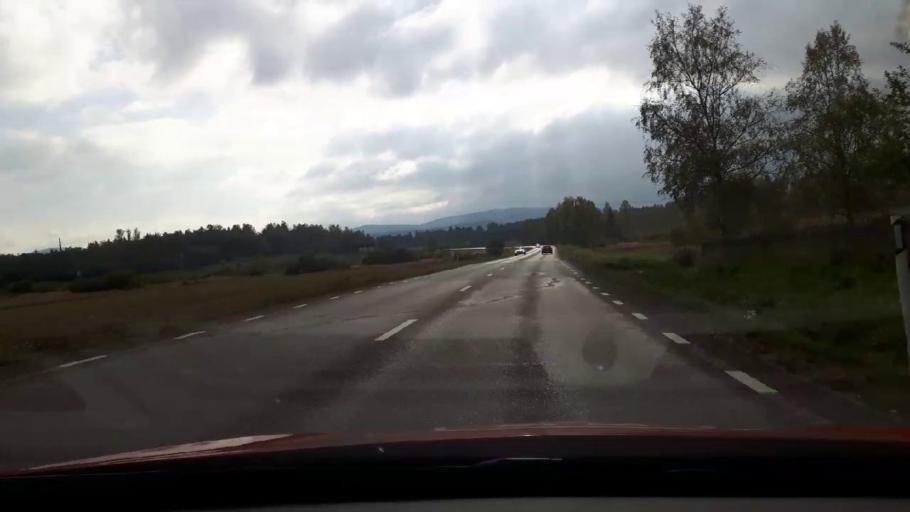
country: SE
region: Gaevleborg
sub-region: Bollnas Kommun
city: Kilafors
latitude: 61.2431
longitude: 16.5504
